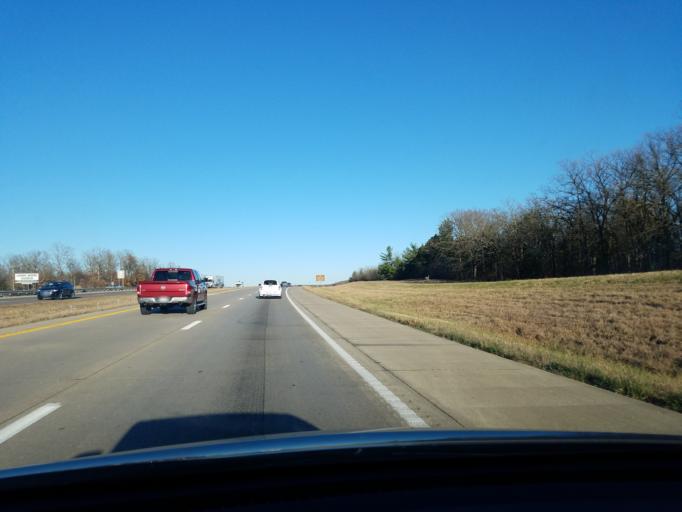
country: US
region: Missouri
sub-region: Crawford County
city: Cuba
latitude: 38.1139
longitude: -91.3275
